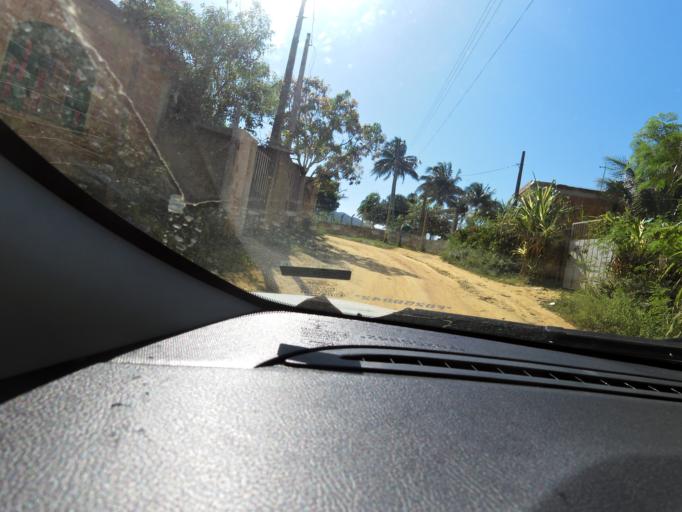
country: BR
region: Espirito Santo
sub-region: Guarapari
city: Guarapari
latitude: -20.6542
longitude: -40.5197
